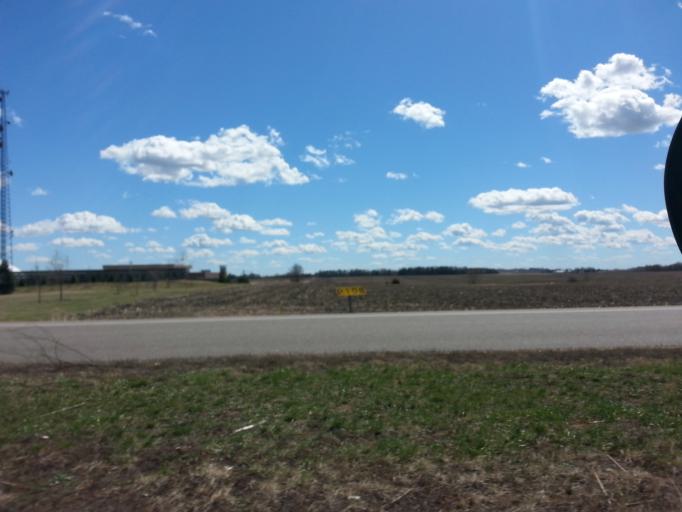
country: US
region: Minnesota
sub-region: Dakota County
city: Rosemount
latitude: 44.7171
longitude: -93.1266
